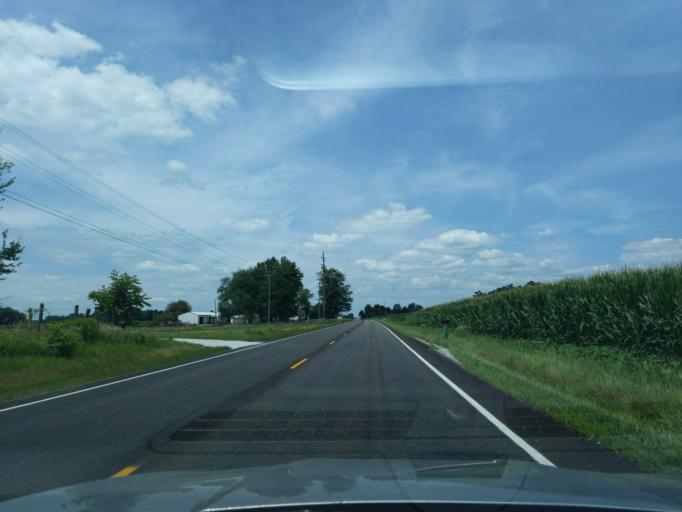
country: US
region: Indiana
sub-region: Ripley County
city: Osgood
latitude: 39.2152
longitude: -85.3330
